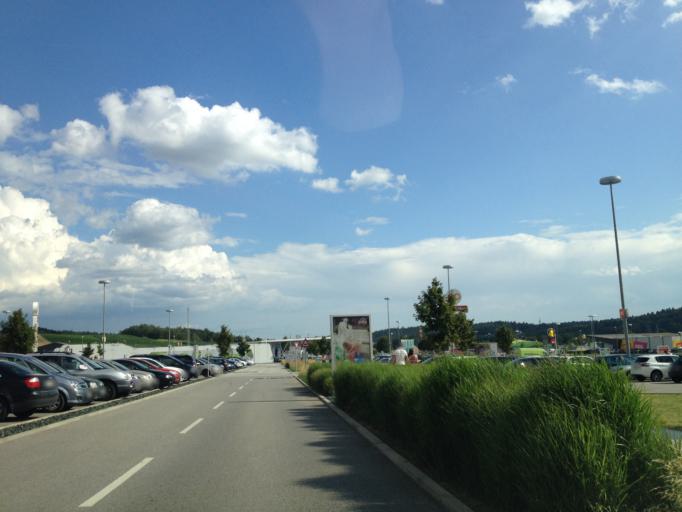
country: AT
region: Burgenland
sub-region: Politischer Bezirk Oberwart
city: Oberwart
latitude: 47.2867
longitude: 16.1867
